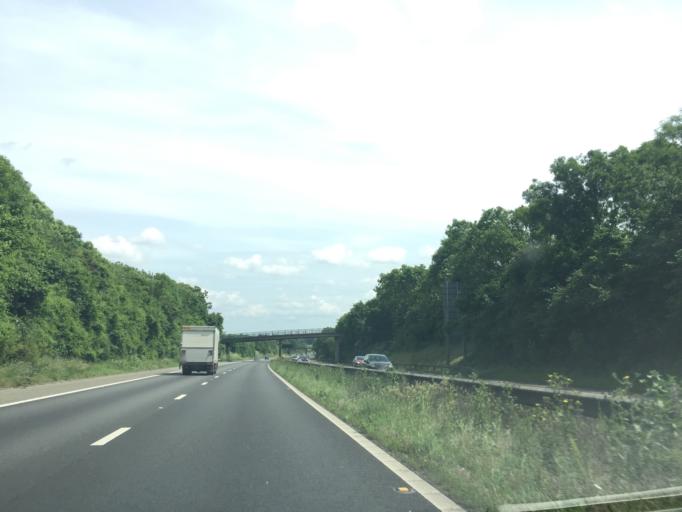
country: GB
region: England
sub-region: Kent
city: Rainham
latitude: 51.3419
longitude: 0.6247
